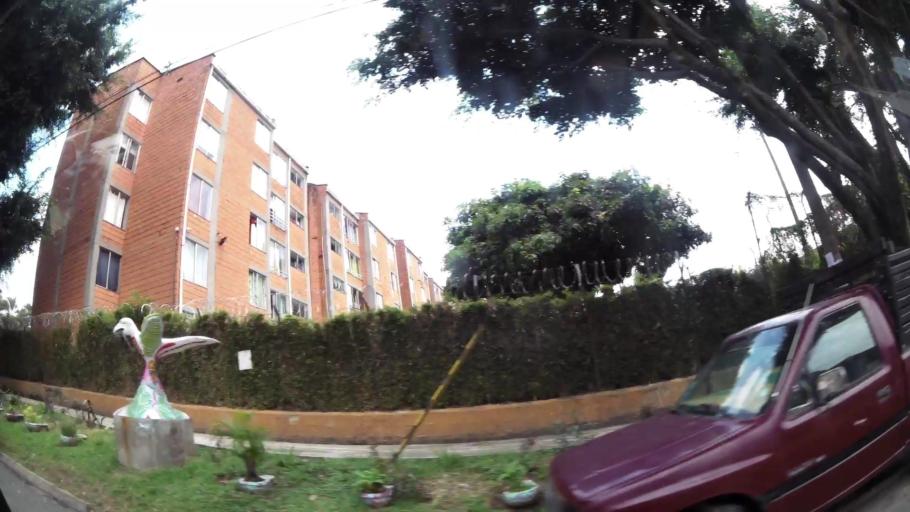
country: CO
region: Antioquia
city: Medellin
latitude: 6.2448
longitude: -75.6193
